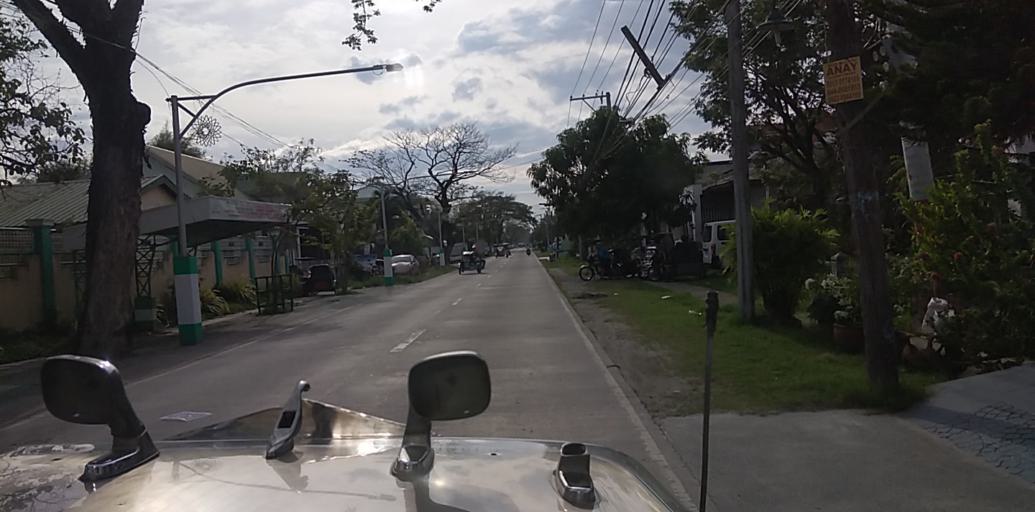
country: PH
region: Central Luzon
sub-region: Province of Pampanga
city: Minalin
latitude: 14.9795
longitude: 120.6922
